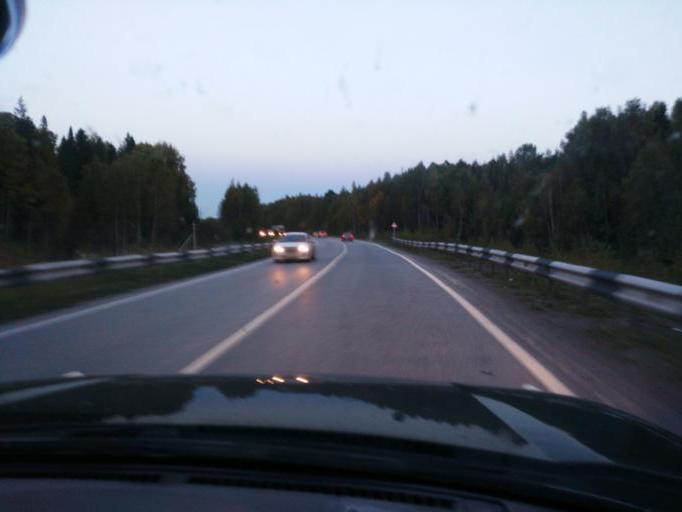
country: RU
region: Perm
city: Verkhnechusovskiye Gorodki
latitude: 58.2454
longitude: 57.0273
